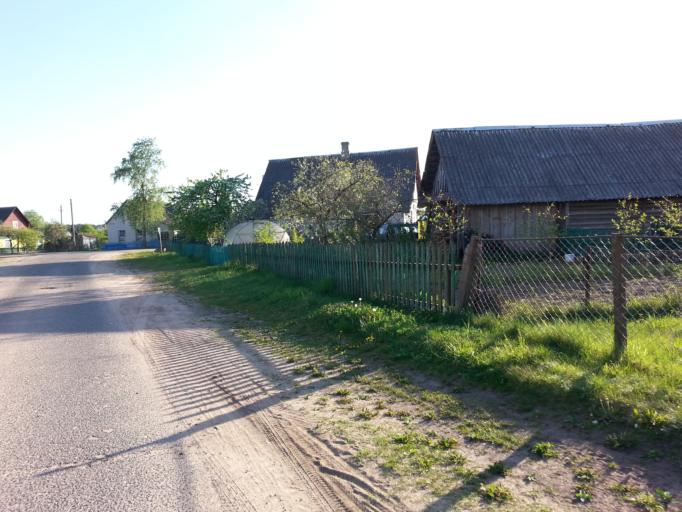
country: BY
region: Minsk
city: Narach
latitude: 54.9324
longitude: 26.6893
